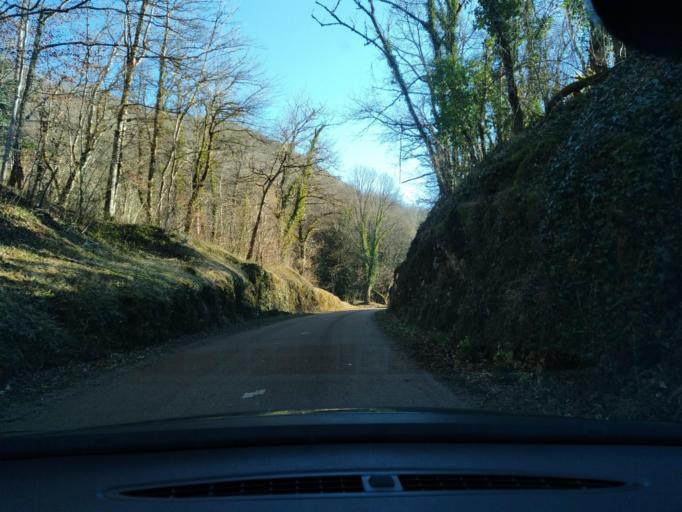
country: FR
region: Franche-Comte
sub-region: Departement du Jura
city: Clairvaux-les-Lacs
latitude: 46.6911
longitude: 5.7281
